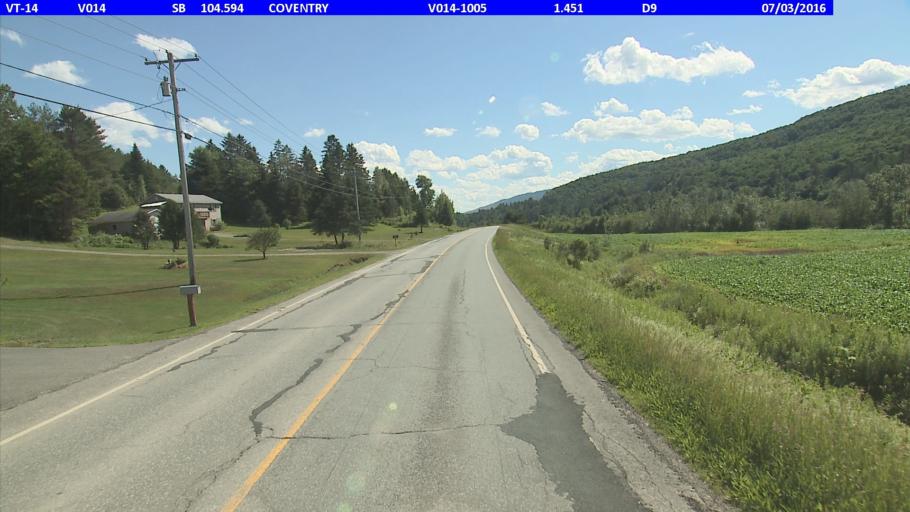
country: US
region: Vermont
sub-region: Orleans County
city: Newport
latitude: 44.8846
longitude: -72.2624
